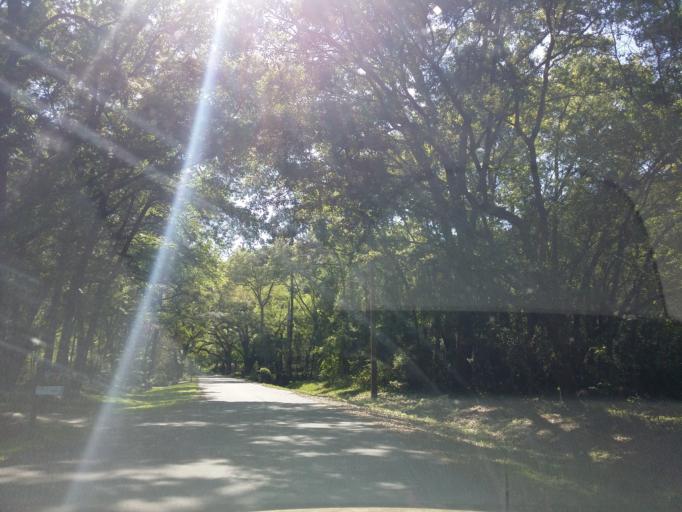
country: US
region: Florida
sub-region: Leon County
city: Tallahassee
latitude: 30.4891
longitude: -84.1864
